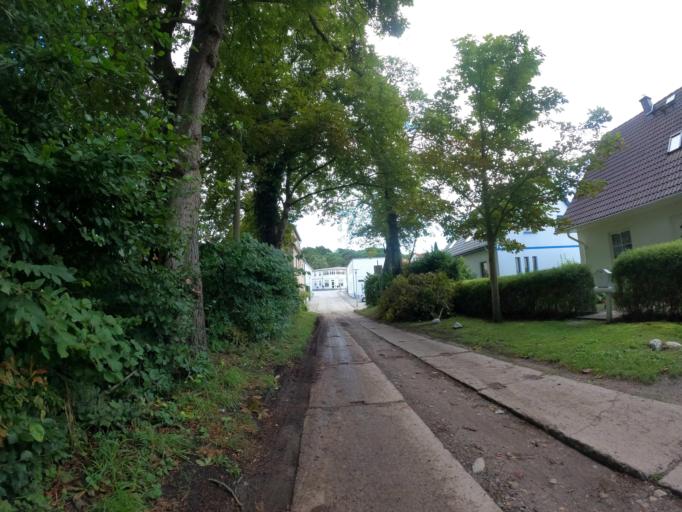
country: DE
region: Mecklenburg-Vorpommern
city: Putbus
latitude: 54.3585
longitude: 13.4702
